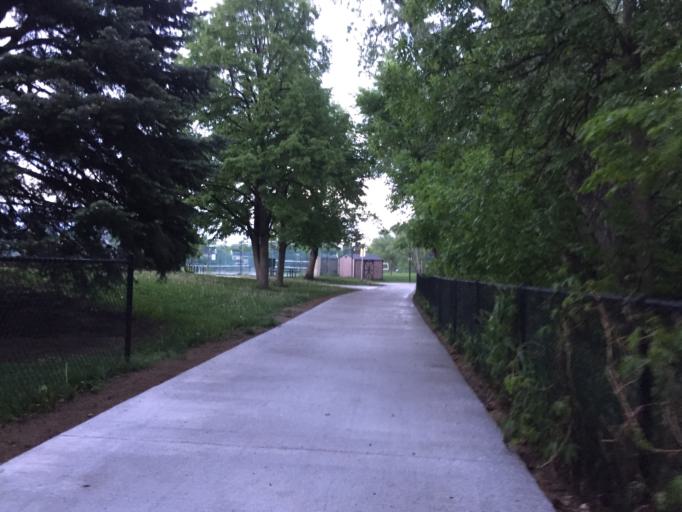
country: US
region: Colorado
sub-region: Boulder County
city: Boulder
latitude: 40.0319
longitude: -105.2797
